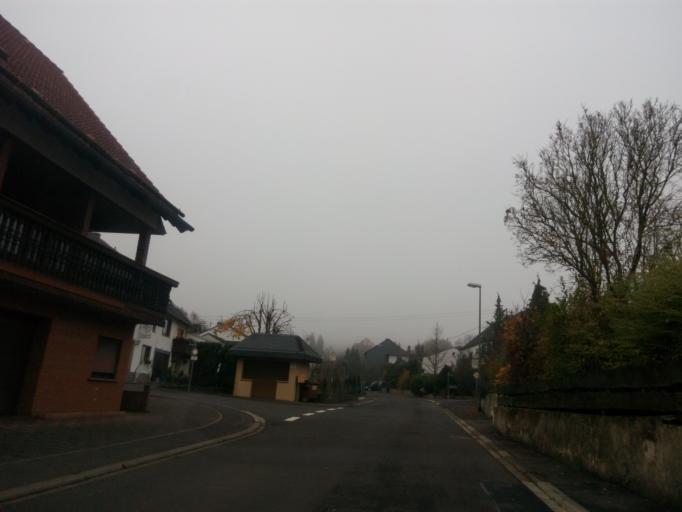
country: DE
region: Rheinland-Pfalz
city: Oberreidenbach
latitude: 49.7057
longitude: 7.4607
